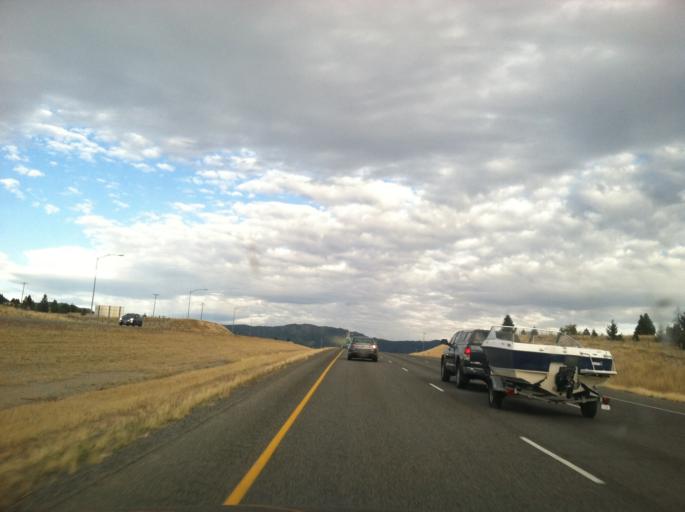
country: US
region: Montana
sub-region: Silver Bow County
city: Butte
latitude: 46.0060
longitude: -112.5980
